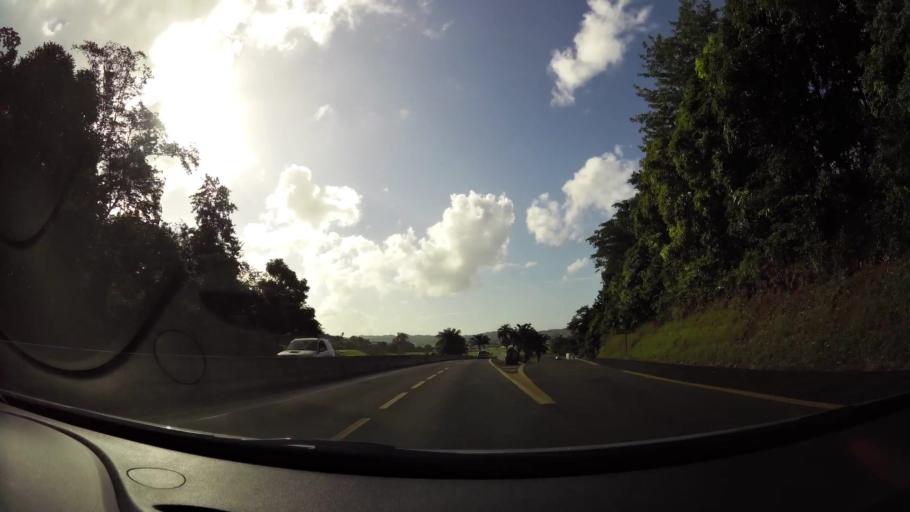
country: MQ
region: Martinique
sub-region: Martinique
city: Ducos
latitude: 14.5556
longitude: -60.9716
